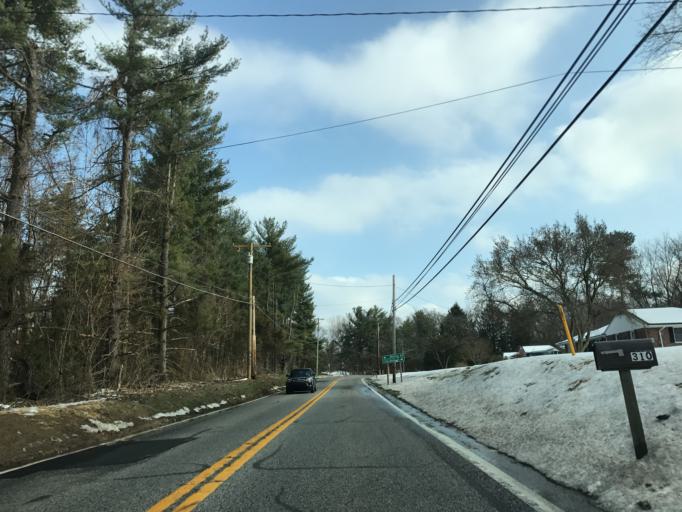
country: US
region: Maryland
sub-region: Harford County
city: South Bel Air
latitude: 39.5738
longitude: -76.2559
